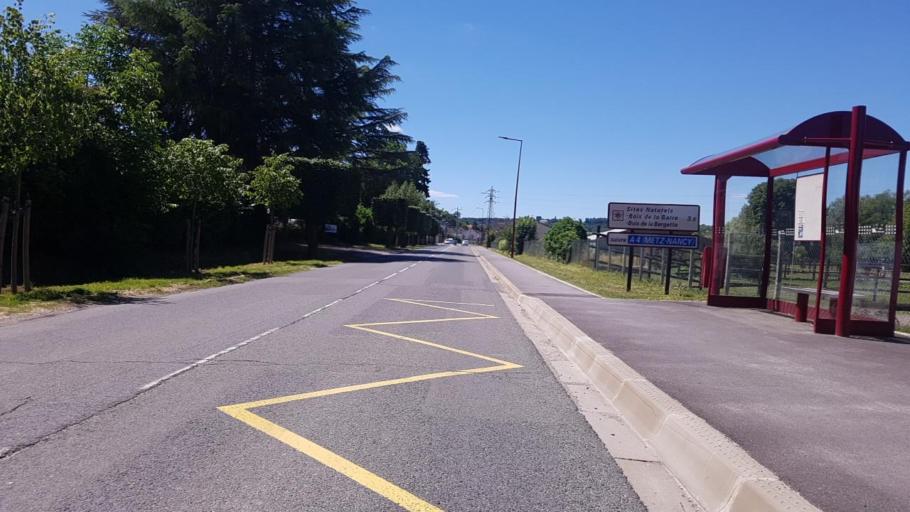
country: FR
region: Ile-de-France
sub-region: Departement de Seine-et-Marne
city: La Ferte-sous-Jouarre
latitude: 48.9547
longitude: 3.1402
